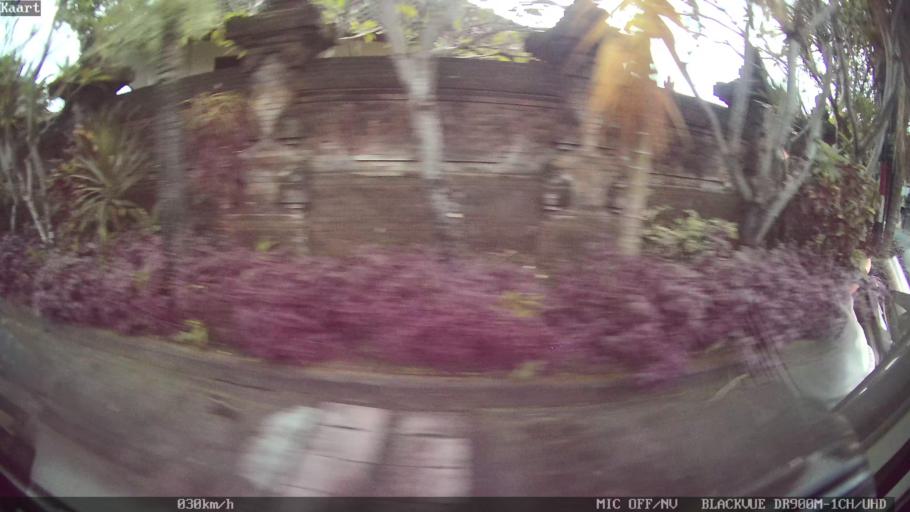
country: ID
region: Bali
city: Banjar Kertasari
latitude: -8.6234
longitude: 115.2029
